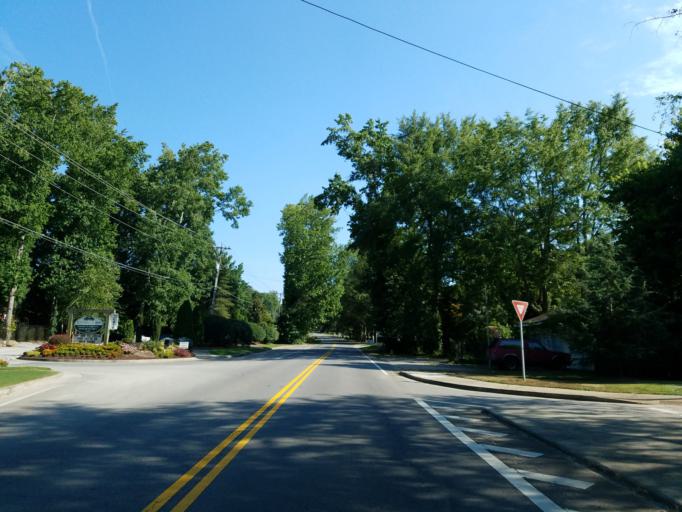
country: US
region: Georgia
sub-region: Fulton County
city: Milton
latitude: 34.1629
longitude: -84.3336
